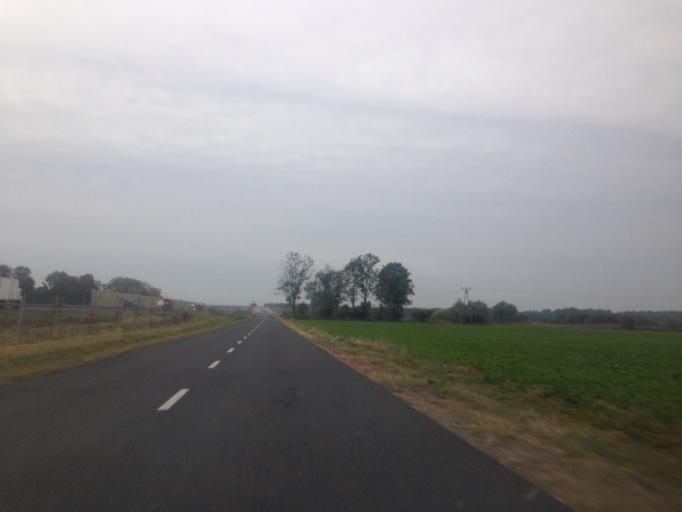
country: PL
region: Greater Poland Voivodeship
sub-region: Powiat gnieznienski
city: Lubowo
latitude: 52.4787
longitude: 17.4149
